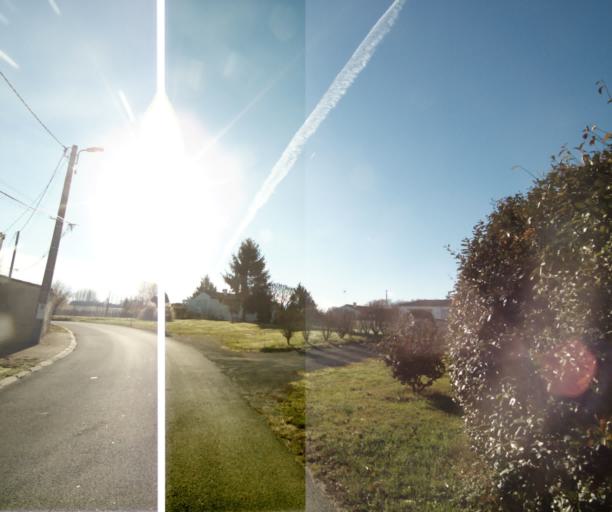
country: FR
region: Poitou-Charentes
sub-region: Departement de la Charente-Maritime
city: Fontcouverte
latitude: 45.7529
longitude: -0.5749
